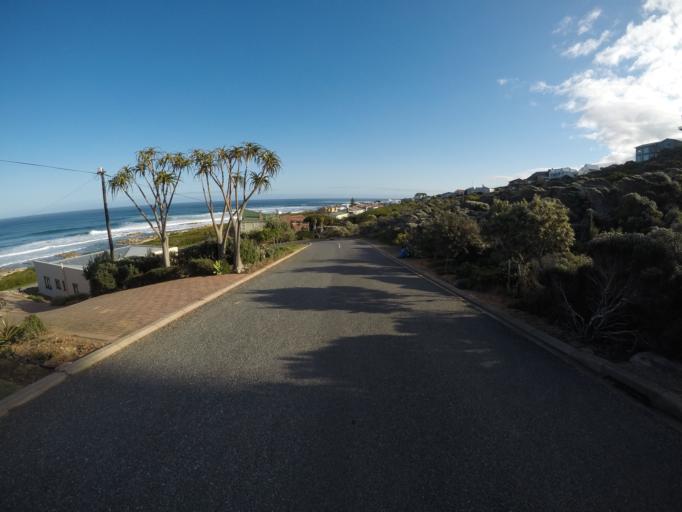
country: ZA
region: Western Cape
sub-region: Eden District Municipality
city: Riversdale
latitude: -34.4213
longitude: 21.3477
